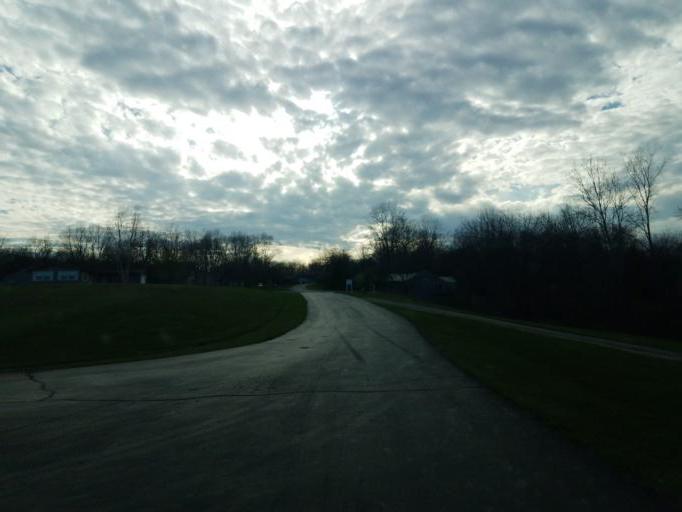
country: US
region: Ohio
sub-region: Knox County
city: Gambier
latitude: 40.4389
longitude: -82.3490
